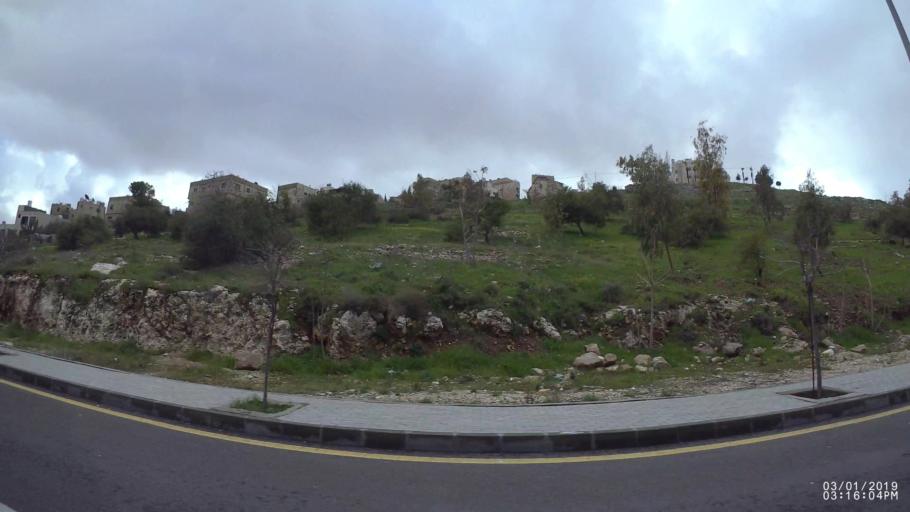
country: JO
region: Amman
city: Amman
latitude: 31.9508
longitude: 35.9005
